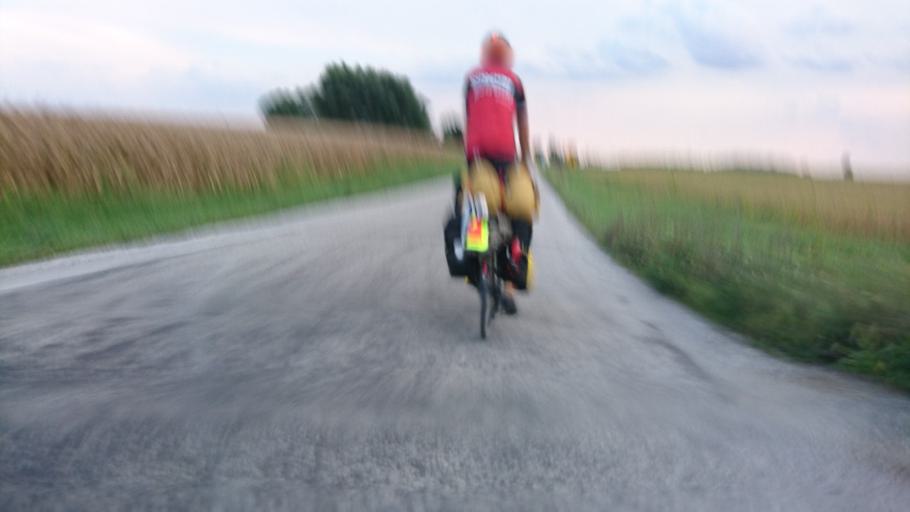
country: US
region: Illinois
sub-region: Logan County
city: Atlanta
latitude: 40.2452
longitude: -89.2051
